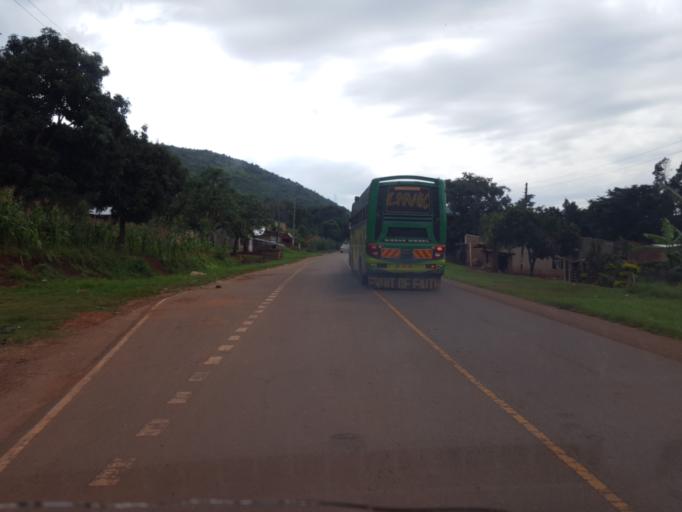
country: UG
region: Central Region
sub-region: Mityana District
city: Mityana
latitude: 0.6713
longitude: 32.0768
